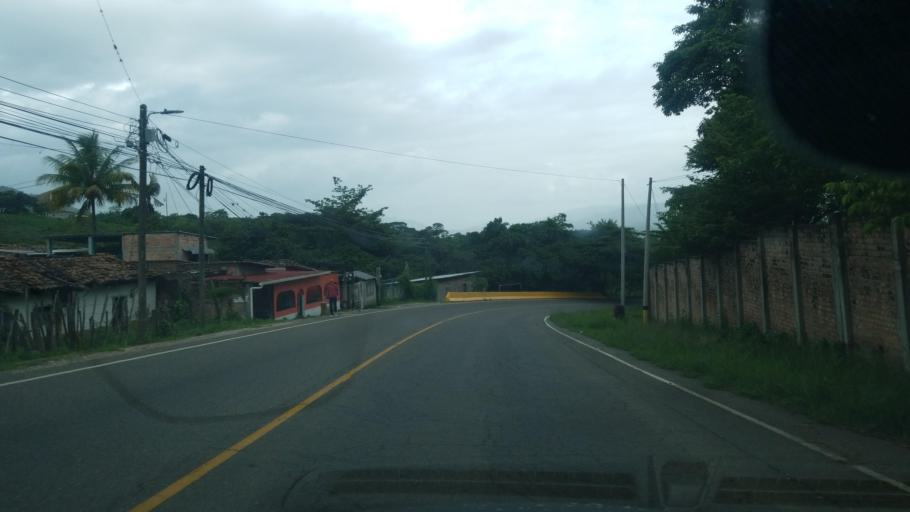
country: HN
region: Ocotepeque
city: Sinuapa
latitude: 14.4460
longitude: -89.1741
